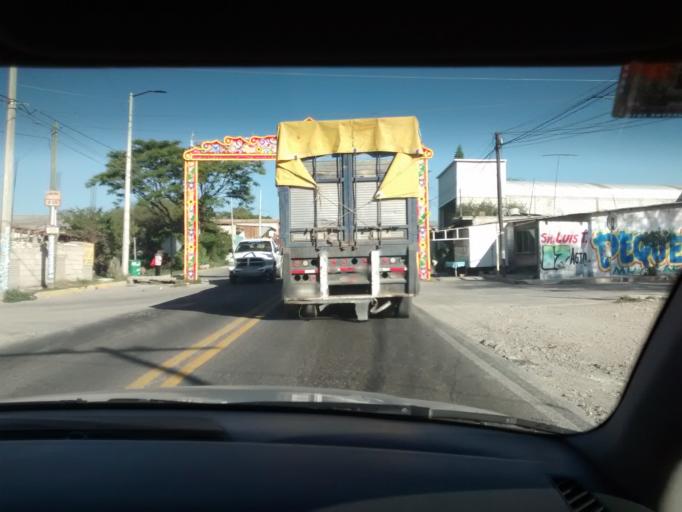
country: MX
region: Puebla
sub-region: Tepanco de Lopez
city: San Andres Cacaloapan
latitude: 18.5526
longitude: -97.5552
